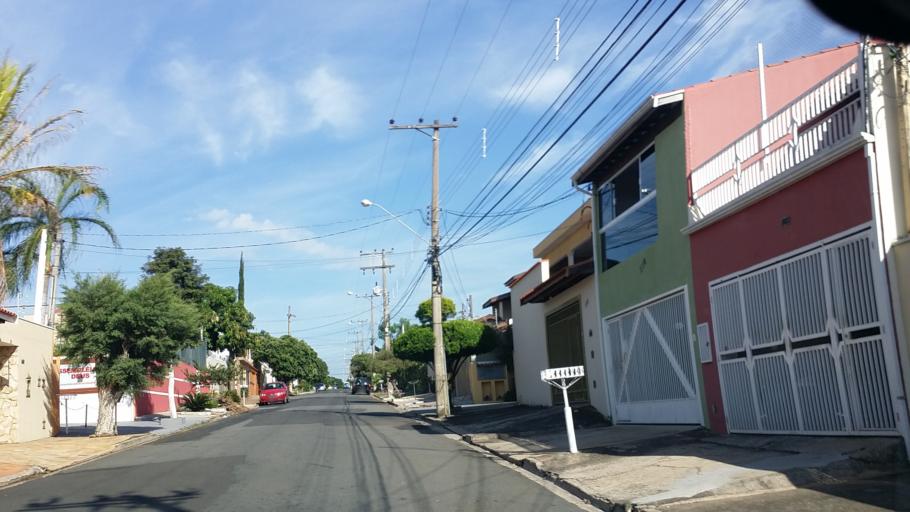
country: BR
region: Sao Paulo
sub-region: Indaiatuba
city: Indaiatuba
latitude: -23.0974
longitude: -47.2313
